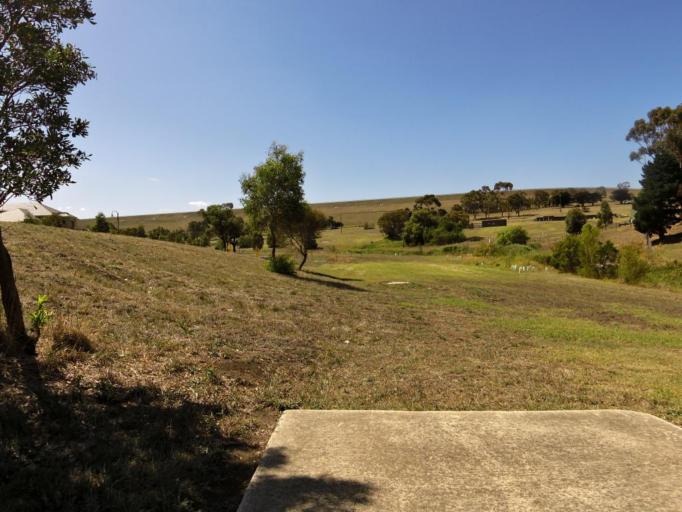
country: AU
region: Victoria
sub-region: Hume
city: Meadow Heights
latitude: -37.6404
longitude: 144.9006
